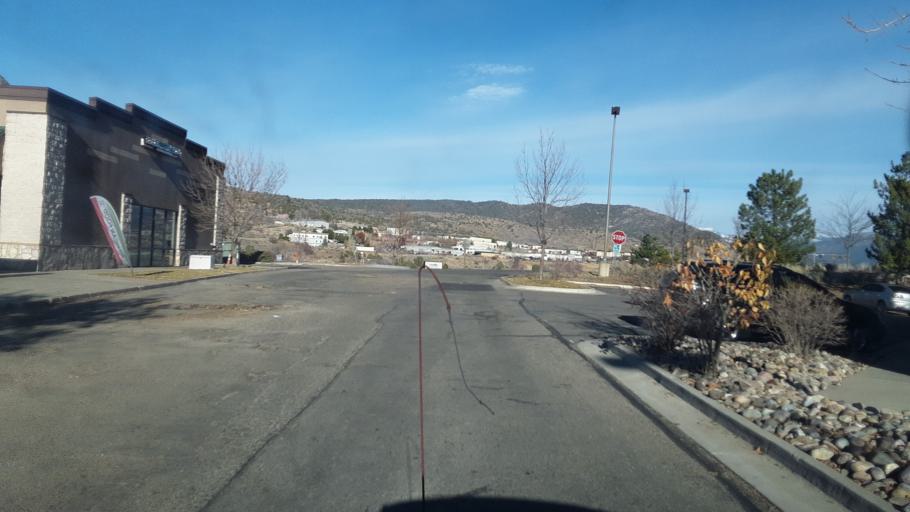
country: US
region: Colorado
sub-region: La Plata County
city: Durango
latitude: 37.2320
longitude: -107.8664
